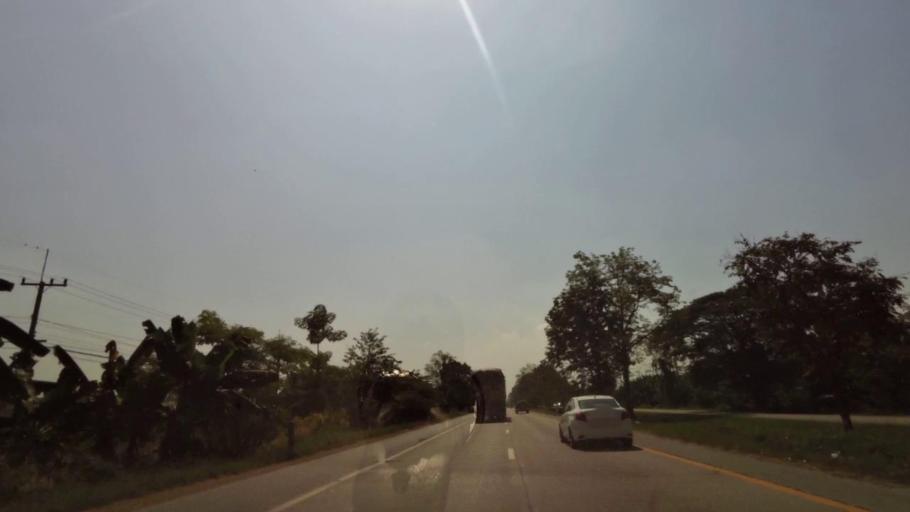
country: TH
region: Phichit
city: Wachira Barami
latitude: 16.6044
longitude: 100.1483
